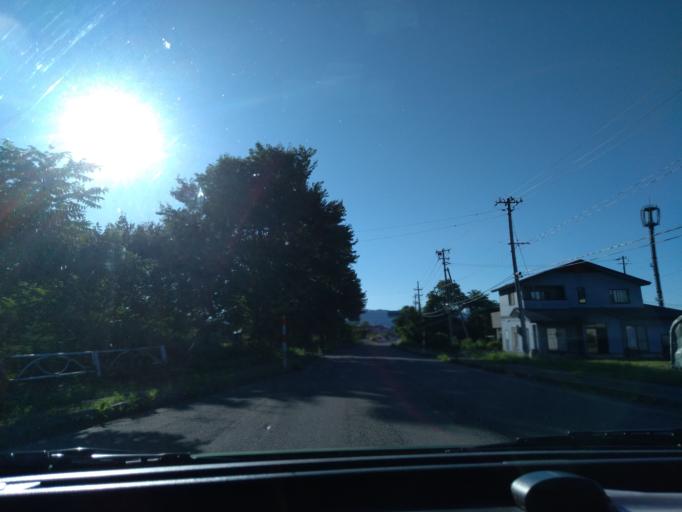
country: JP
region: Akita
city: Omagari
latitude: 39.4262
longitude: 140.4922
